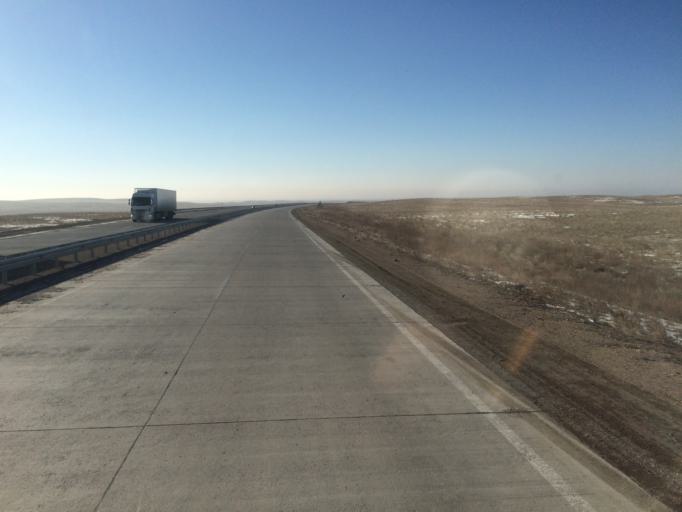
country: KZ
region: Zhambyl
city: Georgiyevka
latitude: 43.3422
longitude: 74.4896
